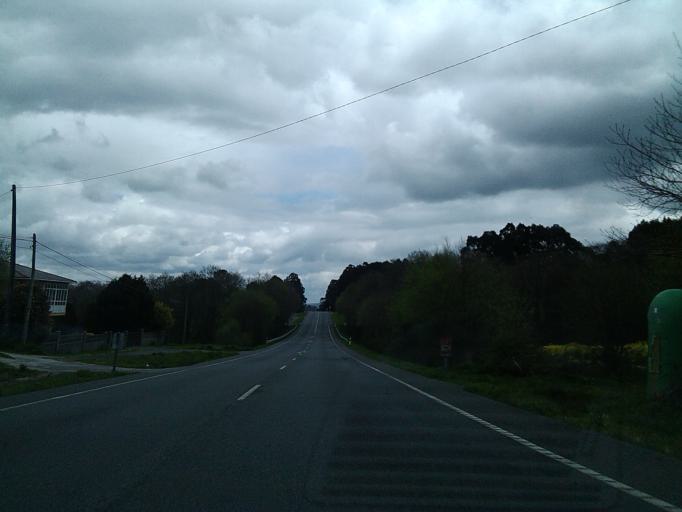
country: ES
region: Galicia
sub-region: Provincia da Coruna
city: Curtis
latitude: 43.1250
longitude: -8.0632
